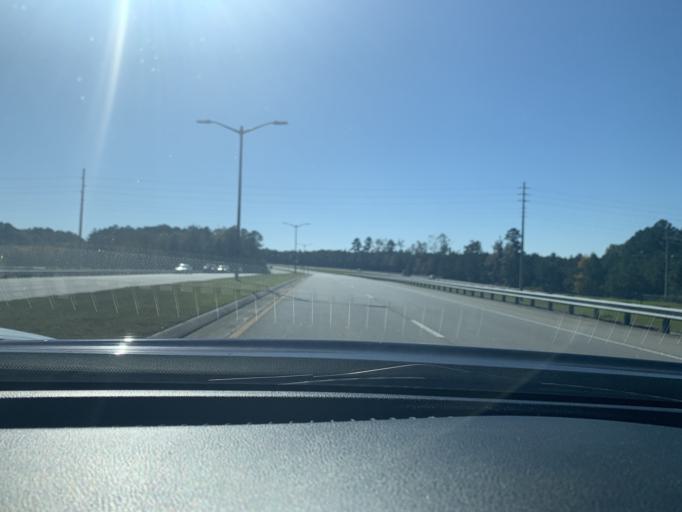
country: US
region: Georgia
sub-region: Chatham County
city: Pooler
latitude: 32.1213
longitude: -81.2681
